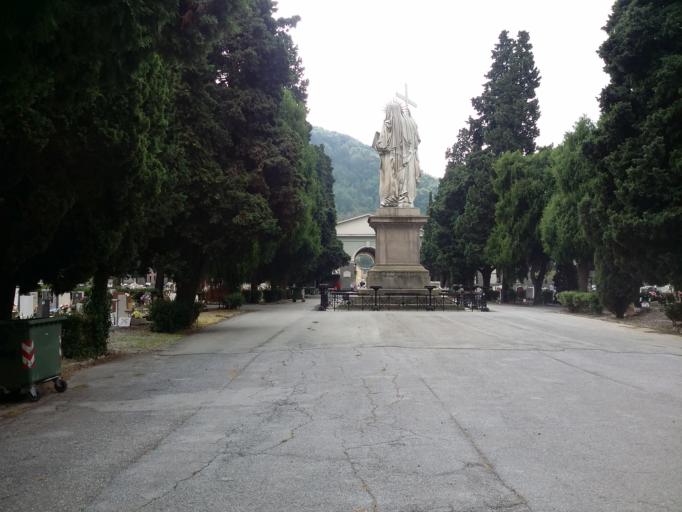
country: IT
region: Liguria
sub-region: Provincia di Genova
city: Genoa
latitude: 44.4295
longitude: 8.9506
